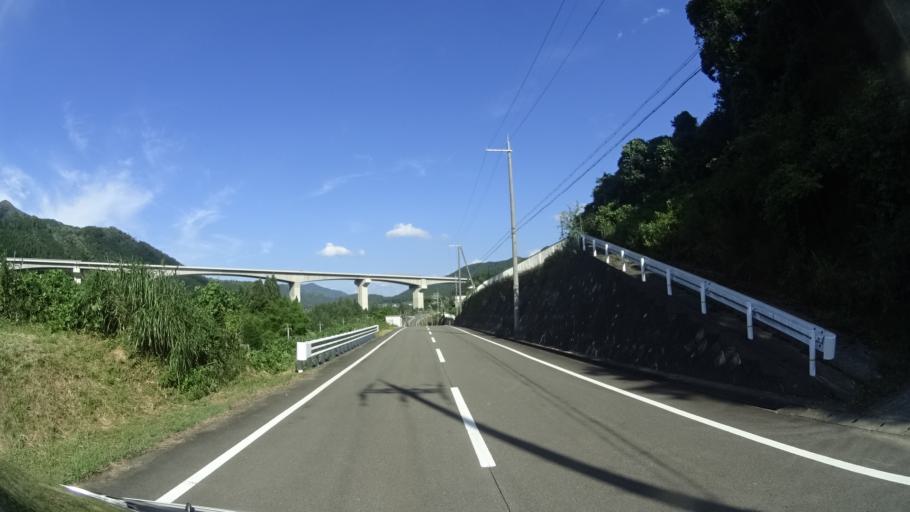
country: JP
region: Kyoto
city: Ayabe
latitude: 35.2745
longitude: 135.3351
